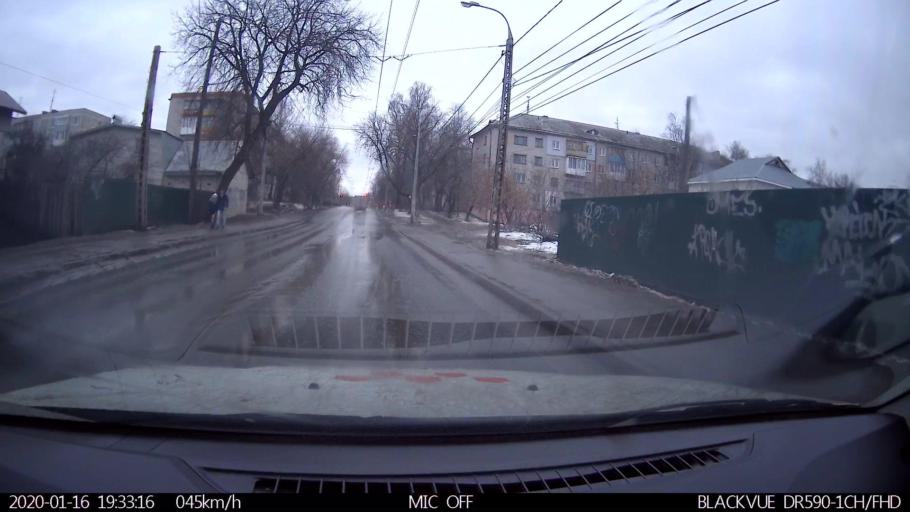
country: RU
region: Nizjnij Novgorod
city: Neklyudovo
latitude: 56.3615
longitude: 43.8459
